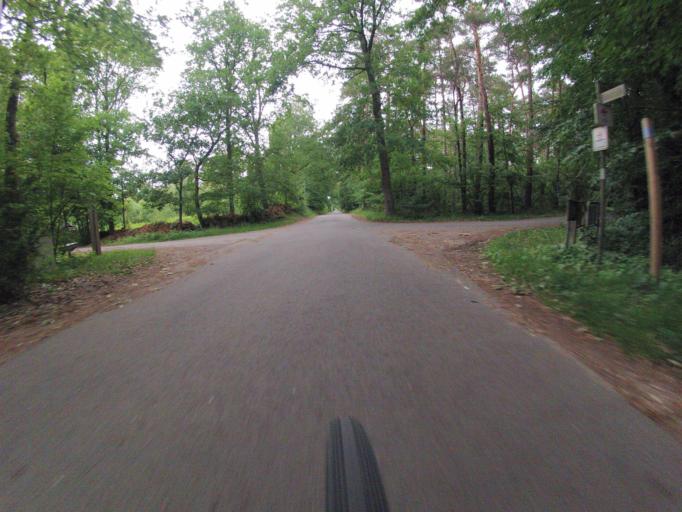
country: DE
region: North Rhine-Westphalia
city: Emsdetten
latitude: 52.2294
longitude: 7.5168
